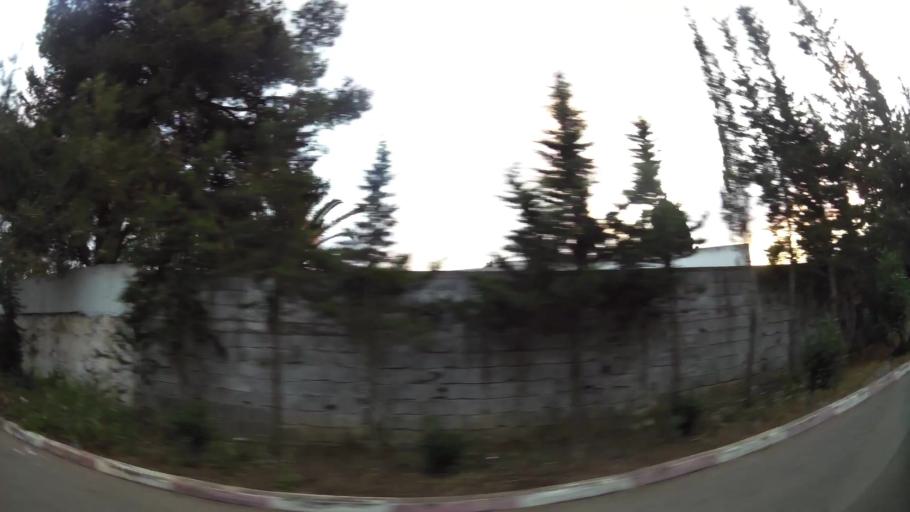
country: MA
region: Rabat-Sale-Zemmour-Zaer
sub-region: Rabat
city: Rabat
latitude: 33.9692
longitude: -6.8379
